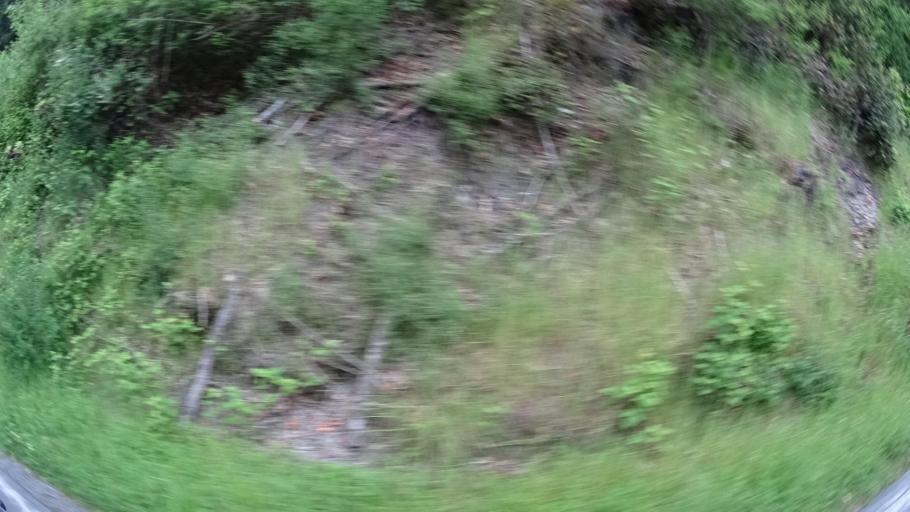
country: US
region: California
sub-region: Humboldt County
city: Willow Creek
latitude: 41.2022
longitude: -123.7506
